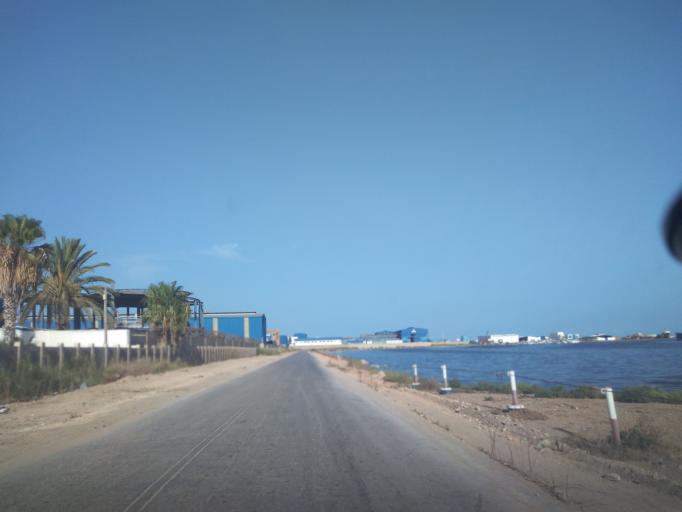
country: TN
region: Safaqis
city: Sfax
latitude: 34.7216
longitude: 10.7615
